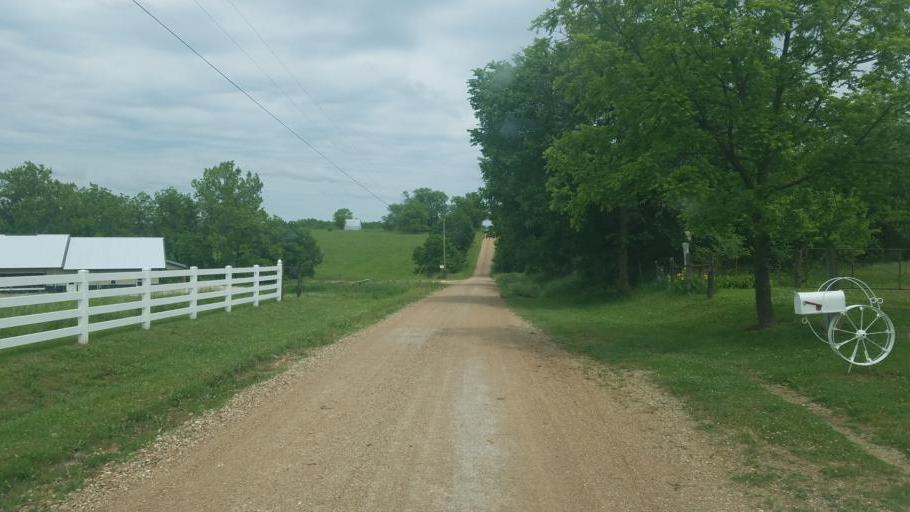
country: US
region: Missouri
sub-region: Moniteau County
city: Tipton
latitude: 38.5514
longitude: -92.7414
